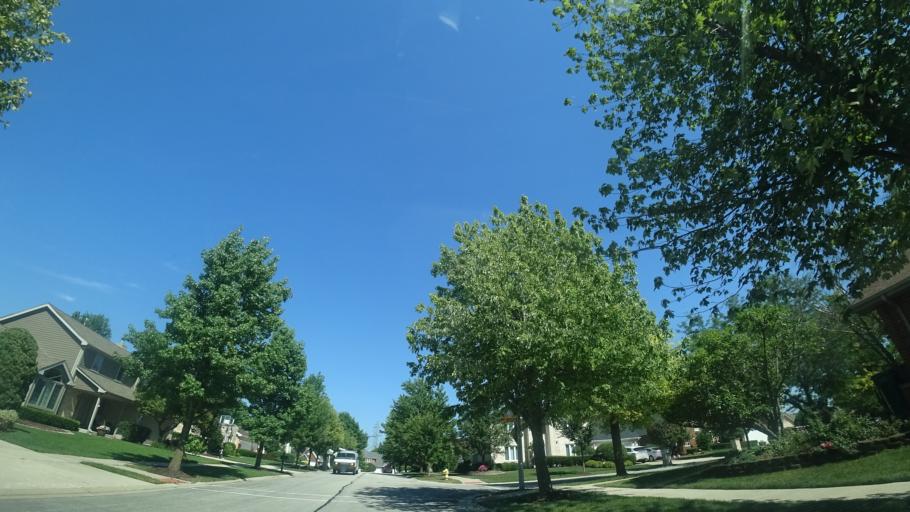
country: US
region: Illinois
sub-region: Will County
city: Mokena
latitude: 41.5711
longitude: -87.8995
